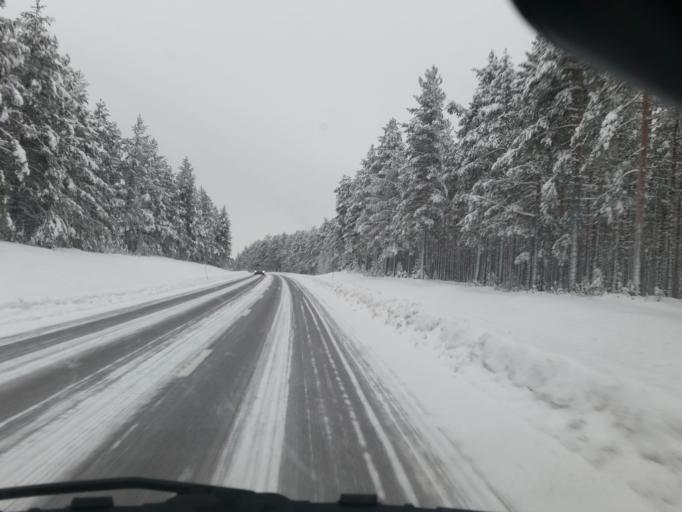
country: SE
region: Norrbotten
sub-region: Pitea Kommun
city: Roknas
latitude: 65.4213
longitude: 21.2866
